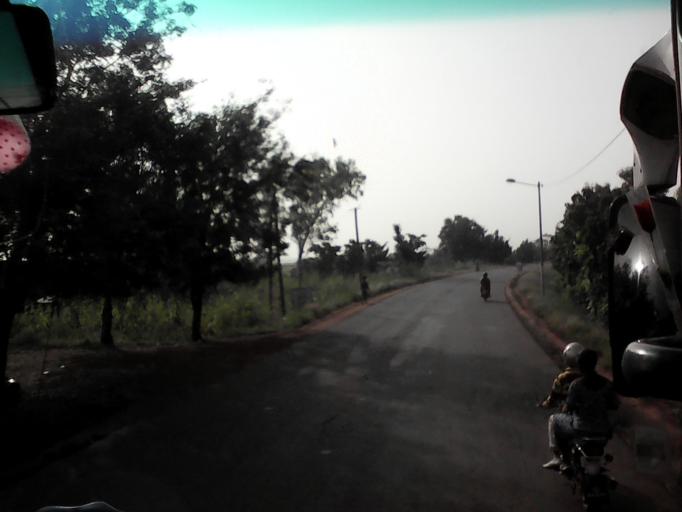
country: TG
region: Kara
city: Kara
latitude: 9.5245
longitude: 1.2068
